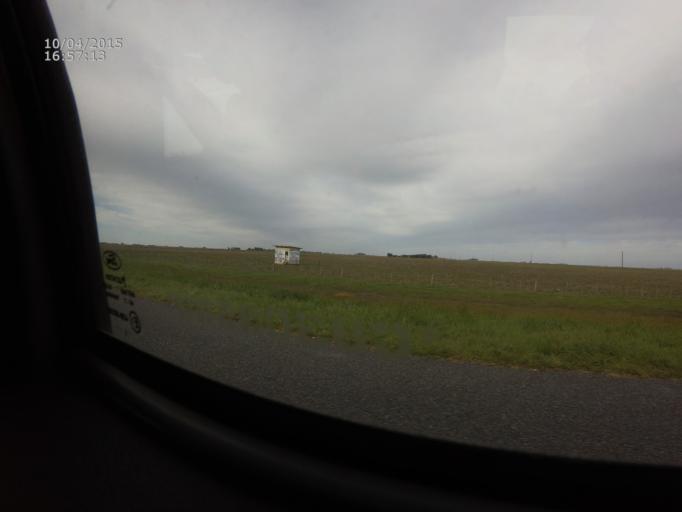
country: AR
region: Buenos Aires
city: Coronel Vidal
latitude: -37.5128
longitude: -57.7108
